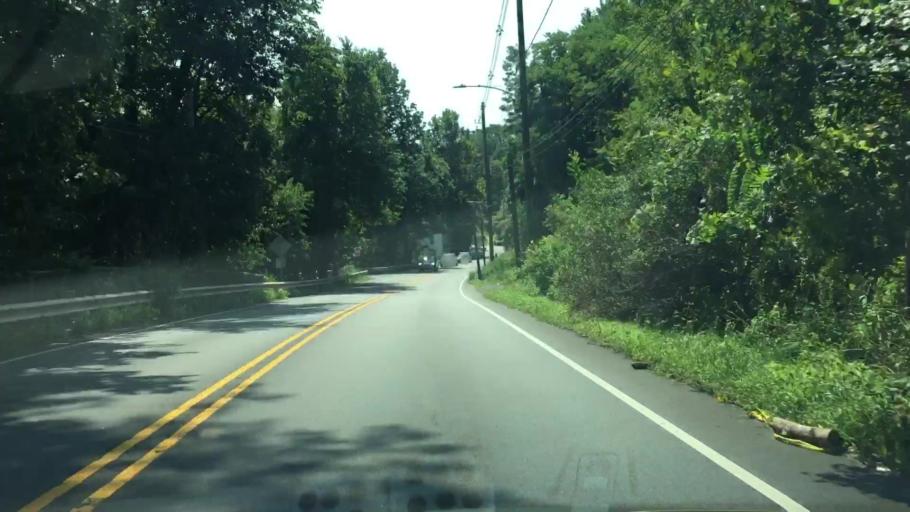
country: US
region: Pennsylvania
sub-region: Delaware County
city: Village Green-Green Ridge
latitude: 39.8880
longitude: -75.4310
